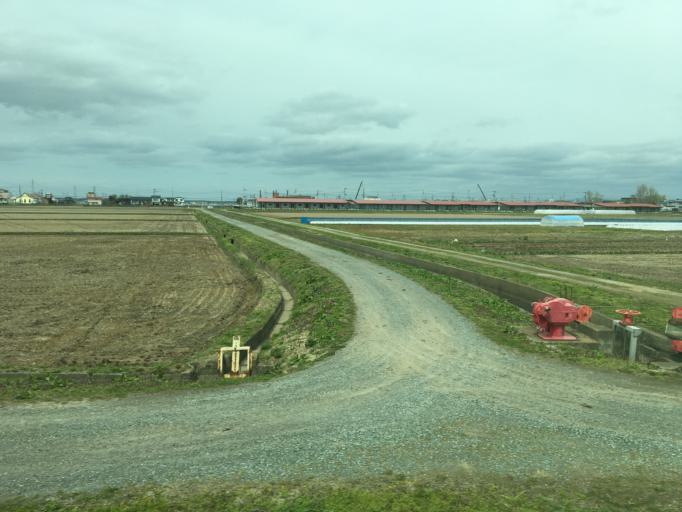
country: JP
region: Aomori
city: Shimokizukuri
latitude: 40.8013
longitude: 140.3848
